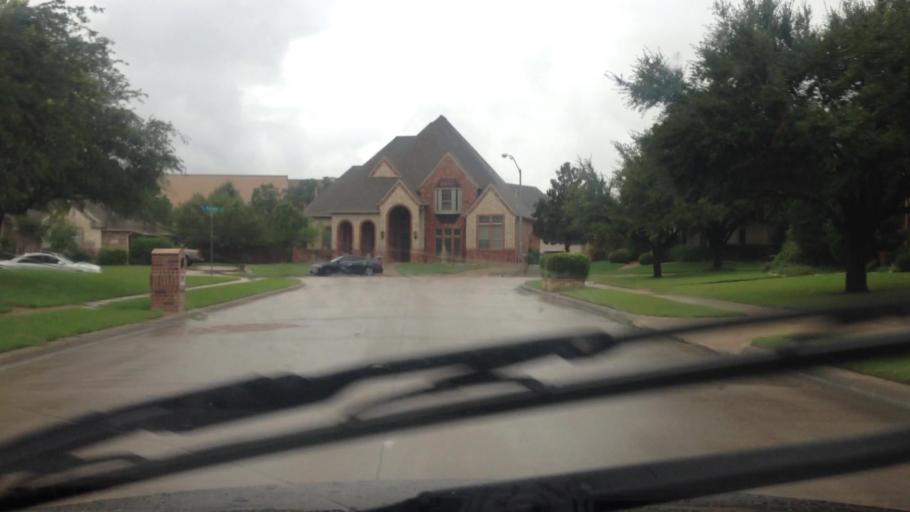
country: US
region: Texas
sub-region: Tarrant County
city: Colleyville
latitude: 32.9003
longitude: -97.1908
